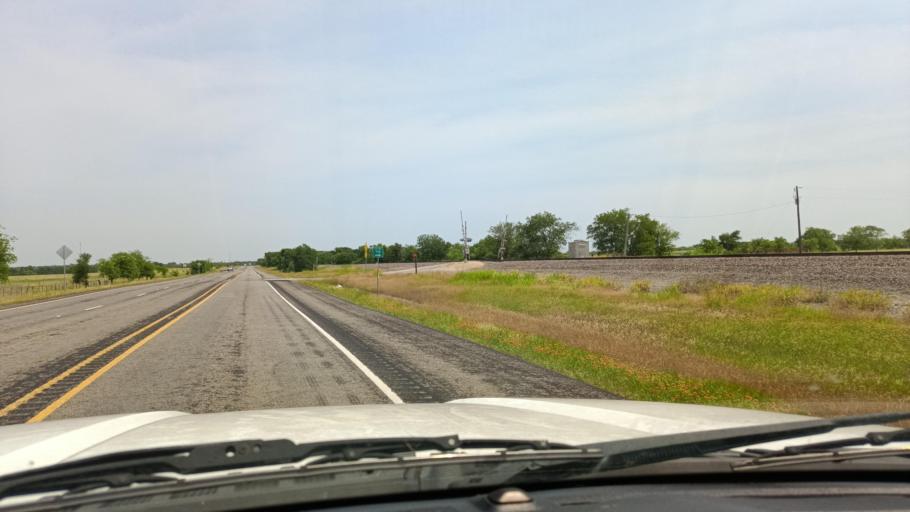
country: US
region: Texas
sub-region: Bell County
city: Rogers
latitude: 30.8907
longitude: -97.1596
